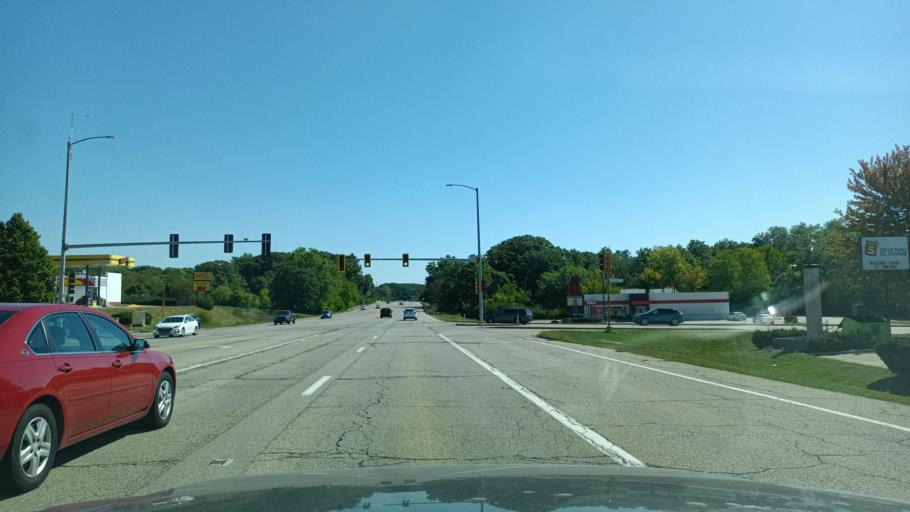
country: US
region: Illinois
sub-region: Peoria County
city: West Peoria
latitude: 40.7704
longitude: -89.6542
